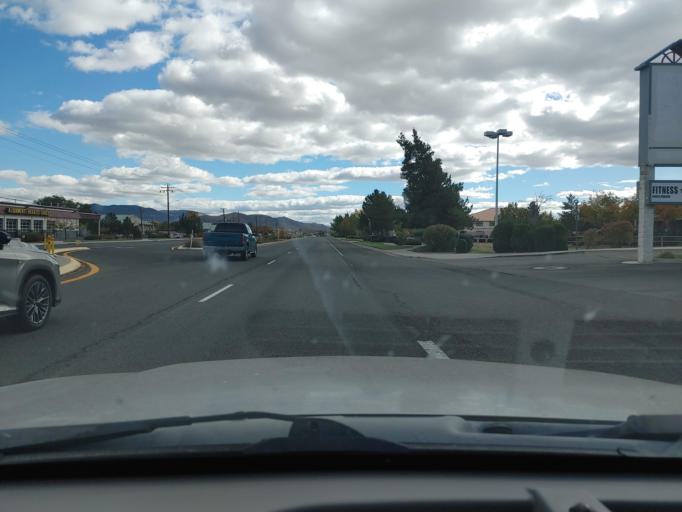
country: US
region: Nevada
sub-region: Carson City
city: Carson City
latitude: 39.1888
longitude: -119.7722
